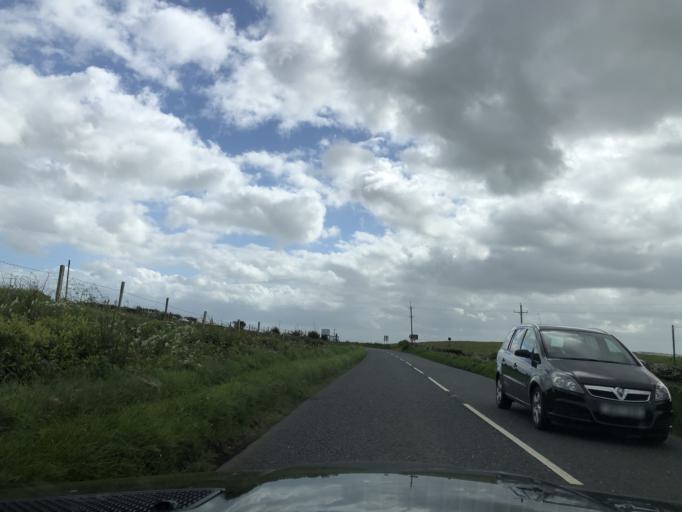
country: GB
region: Northern Ireland
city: Bushmills
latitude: 55.2284
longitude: -6.5166
